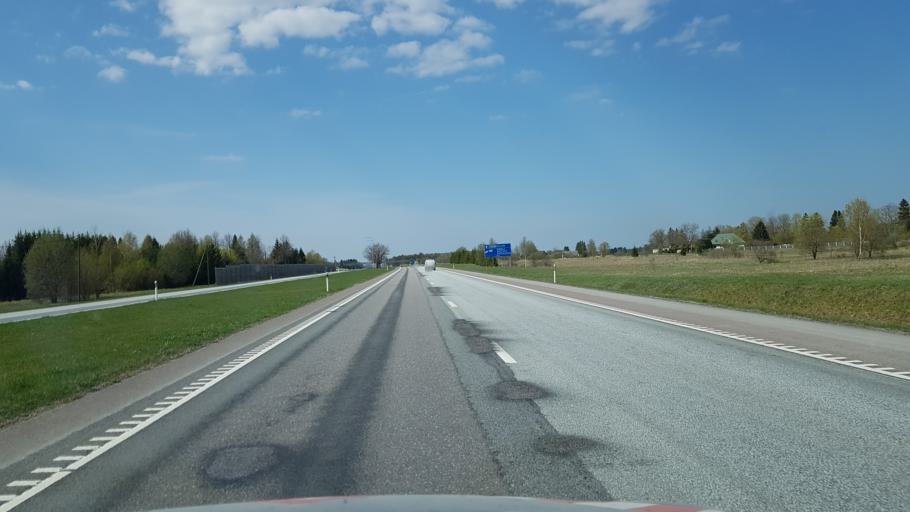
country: EE
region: Harju
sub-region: Rae vald
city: Vaida
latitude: 59.3073
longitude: 24.9415
